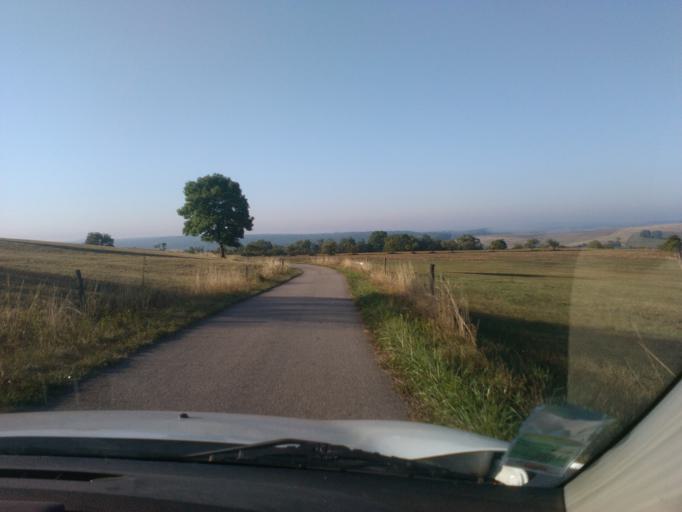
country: FR
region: Lorraine
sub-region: Departement des Vosges
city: Mirecourt
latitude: 48.2636
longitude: 6.1839
